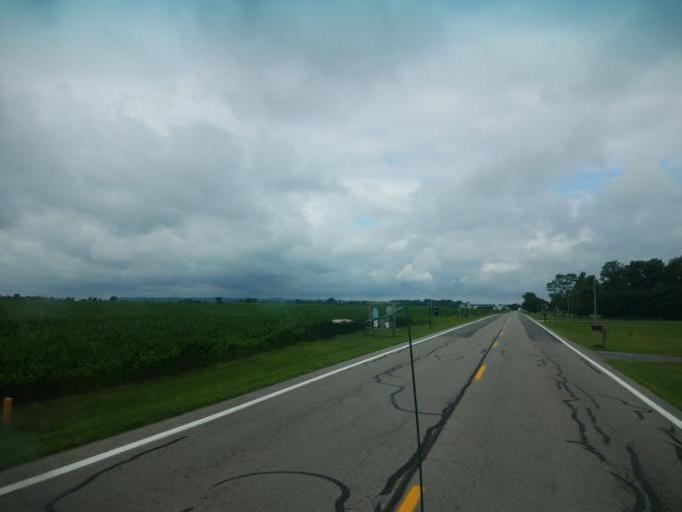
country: US
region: Ohio
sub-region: Champaign County
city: North Lewisburg
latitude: 40.4056
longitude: -83.5511
